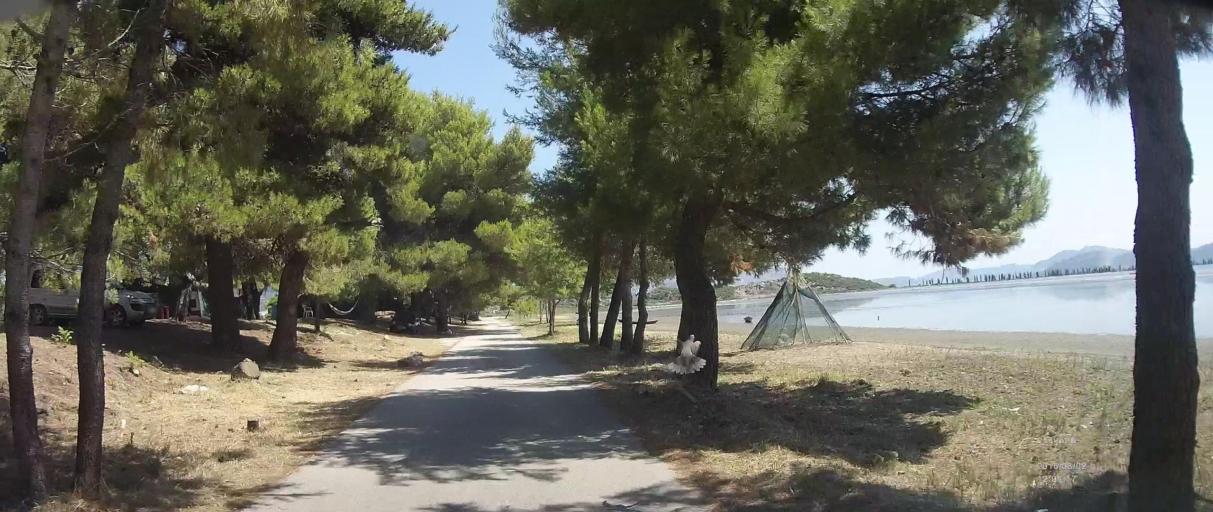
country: HR
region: Dubrovacko-Neretvanska
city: Komin
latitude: 43.0208
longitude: 17.4493
